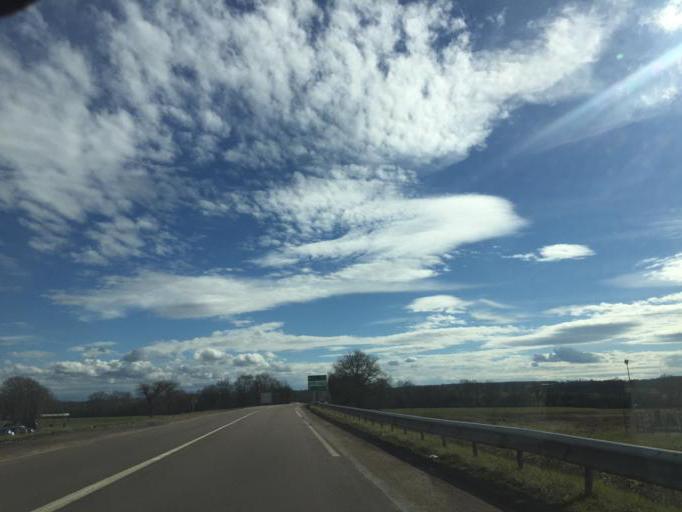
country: FR
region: Bourgogne
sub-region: Departement de l'Yonne
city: Avallon
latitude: 47.5074
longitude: 3.9921
